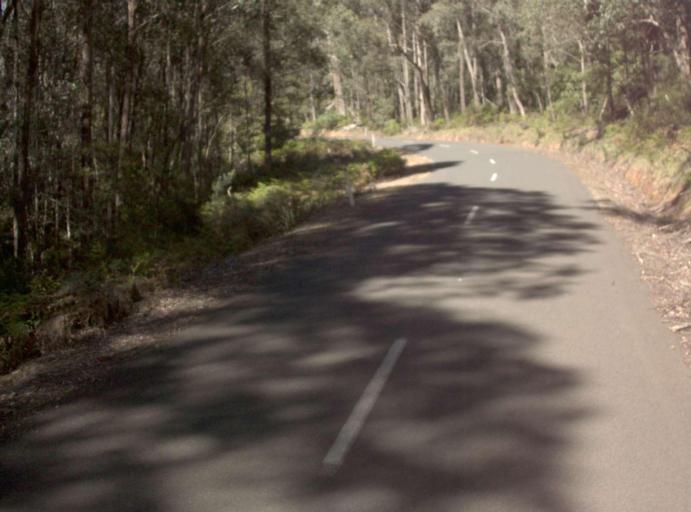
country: AU
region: New South Wales
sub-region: Bombala
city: Bombala
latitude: -37.0735
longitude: 148.7811
